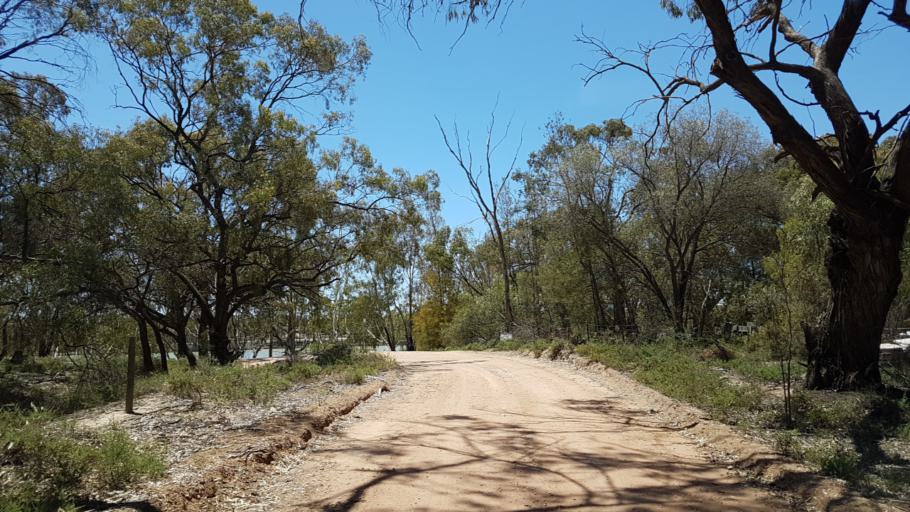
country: AU
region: South Australia
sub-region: Loxton Waikerie
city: Waikerie
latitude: -34.1631
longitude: 140.0331
